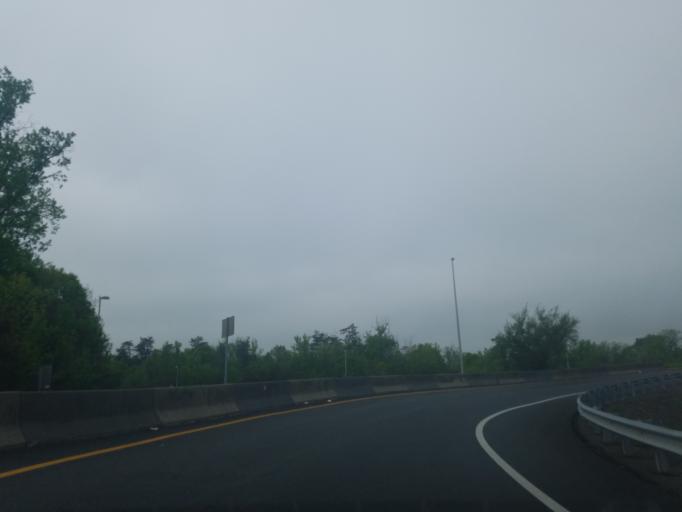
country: US
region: Virginia
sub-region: Fairfax County
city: Vienna
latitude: 38.8776
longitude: -77.2654
